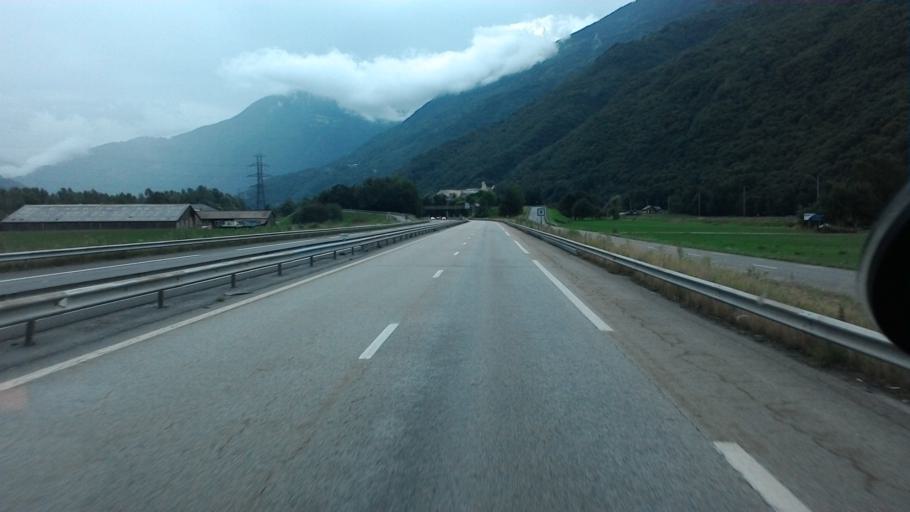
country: FR
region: Rhone-Alpes
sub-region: Departement de la Savoie
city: La Bathie
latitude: 45.6053
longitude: 6.4504
